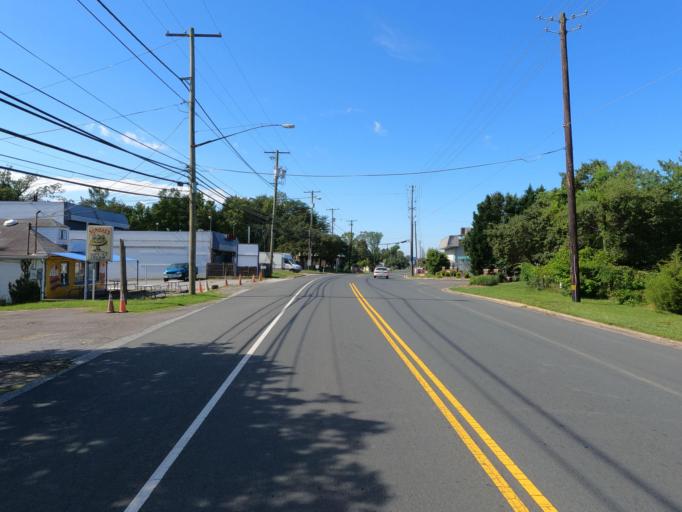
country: US
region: Maryland
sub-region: Prince George's County
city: Oxon Hill
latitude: 38.7883
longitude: -76.9898
